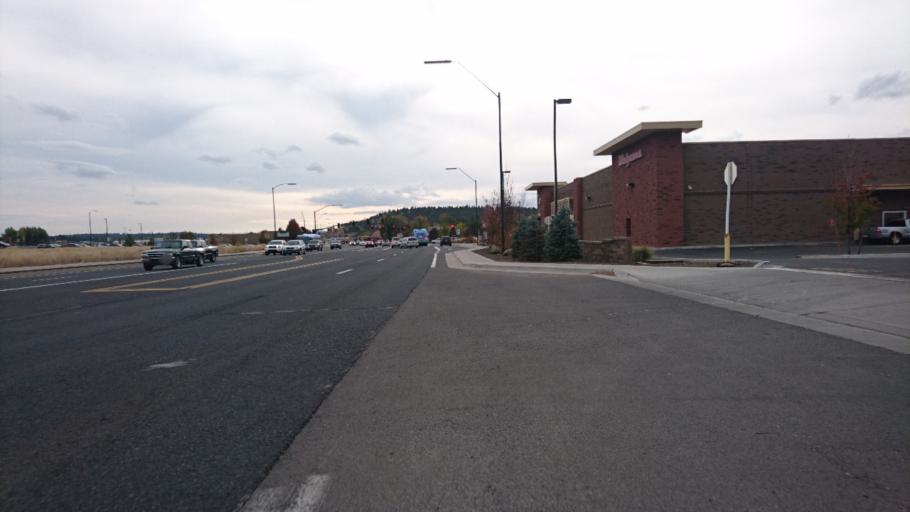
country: US
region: Arizona
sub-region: Coconino County
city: Flagstaff
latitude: 35.2073
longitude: -111.6116
